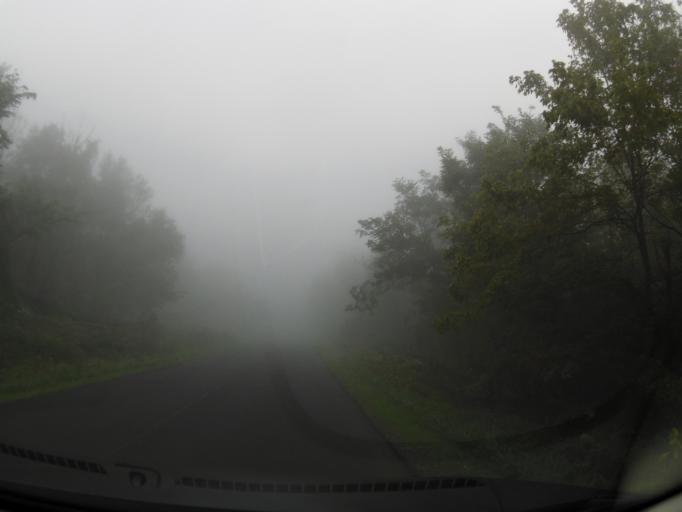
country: US
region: Virginia
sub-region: Page County
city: Luray
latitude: 38.6963
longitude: -78.3198
